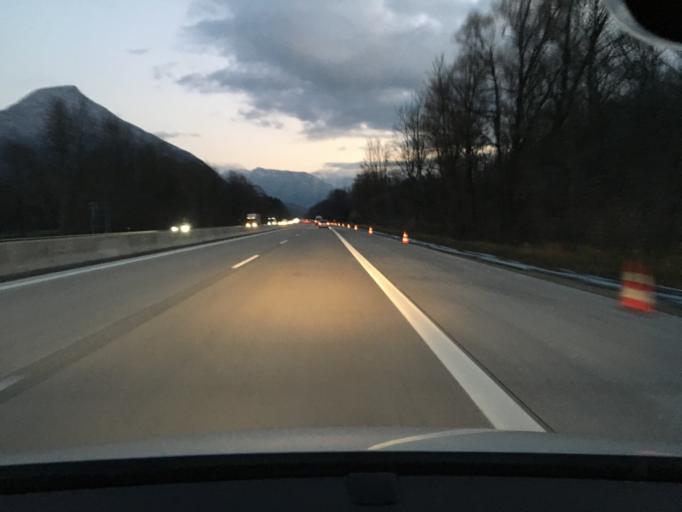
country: DE
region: Bavaria
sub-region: Upper Bavaria
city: Flintsbach
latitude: 47.7234
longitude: 12.1391
